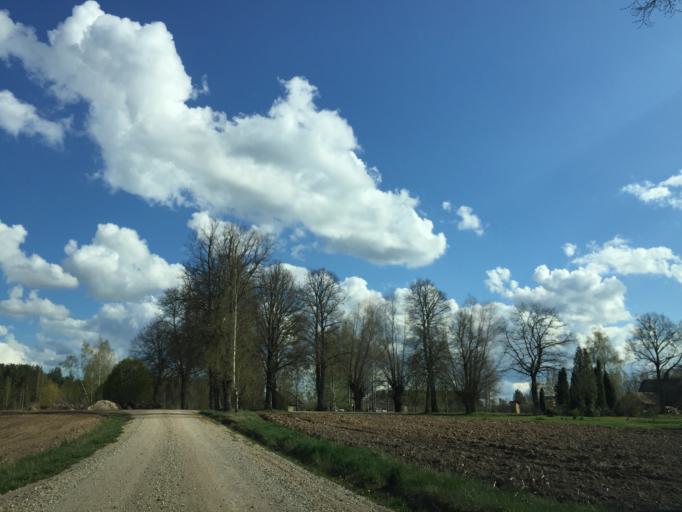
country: LV
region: Beverina
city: Murmuiza
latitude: 57.4195
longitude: 25.5514
